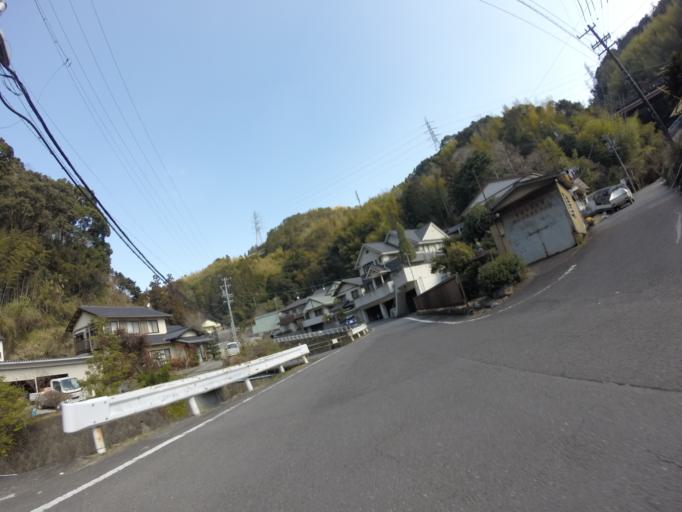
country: JP
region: Shizuoka
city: Shizuoka-shi
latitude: 35.0598
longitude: 138.4975
